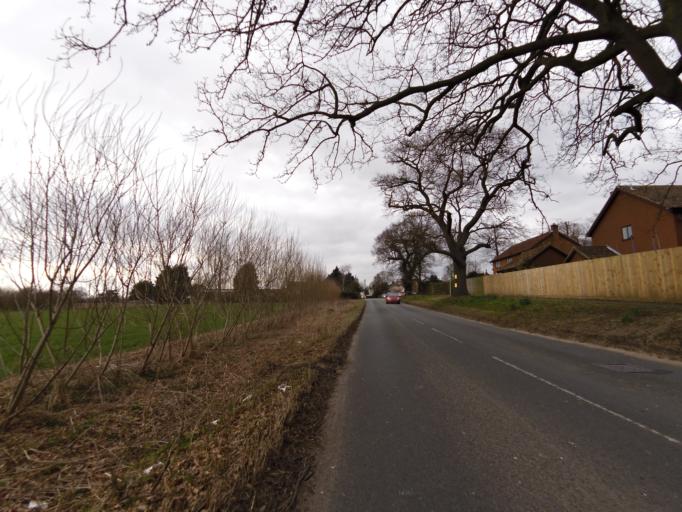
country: GB
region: England
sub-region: Suffolk
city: Ipswich
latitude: 52.1171
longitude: 1.1505
